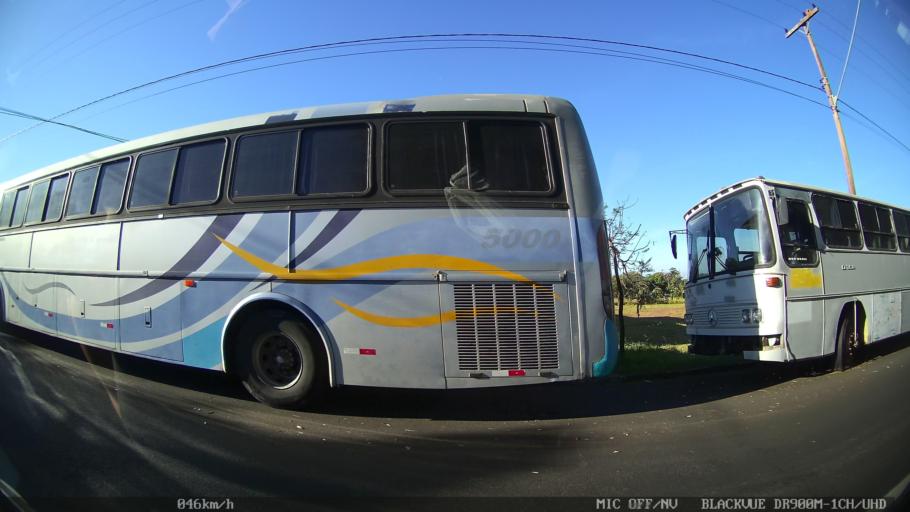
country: BR
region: Sao Paulo
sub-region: Franca
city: Franca
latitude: -20.5820
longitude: -47.3816
